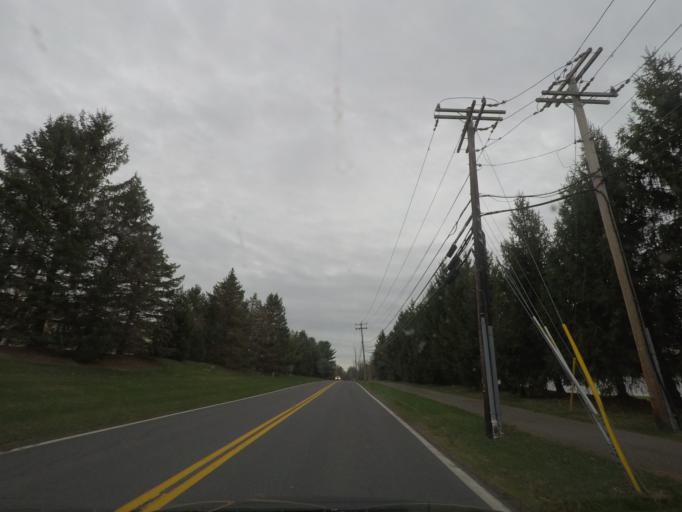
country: US
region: New York
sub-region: Albany County
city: Delmar
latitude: 42.5963
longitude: -73.8114
